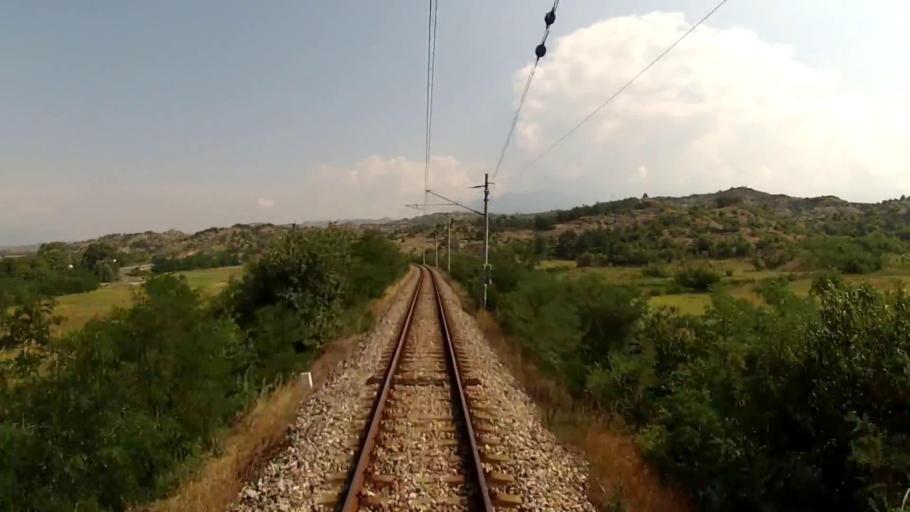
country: BG
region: Blagoevgrad
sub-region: Obshtina Strumyani
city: Strumyani
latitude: 41.6011
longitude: 23.2258
